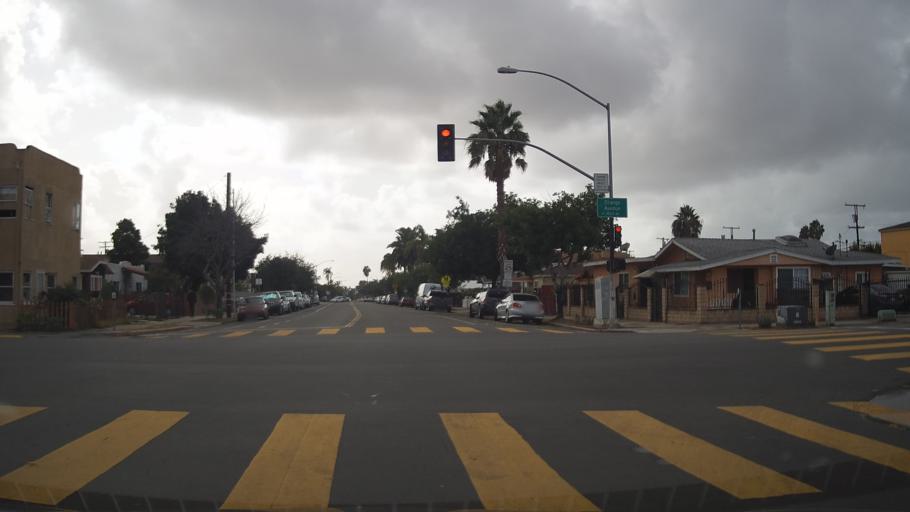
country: US
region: California
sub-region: San Diego County
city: San Diego
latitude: 32.7535
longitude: -117.1180
